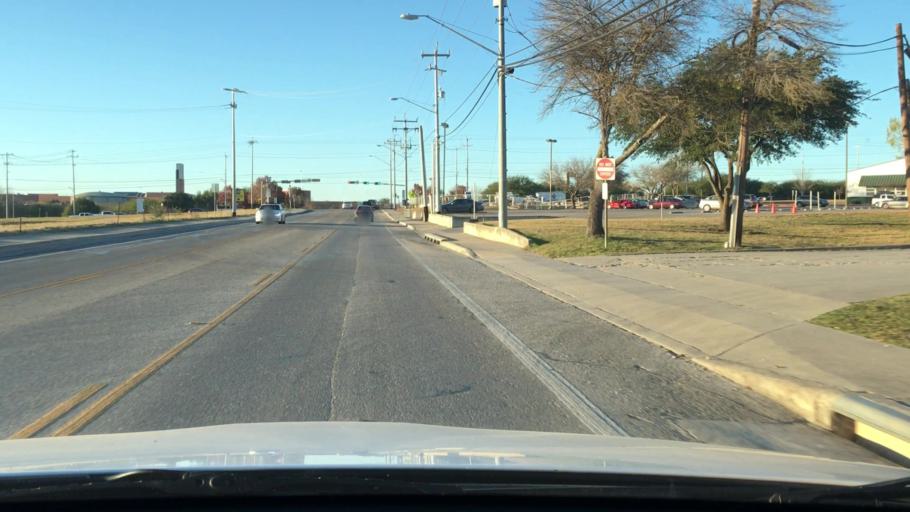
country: US
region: Texas
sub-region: Bexar County
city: Converse
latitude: 29.5425
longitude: -98.3194
